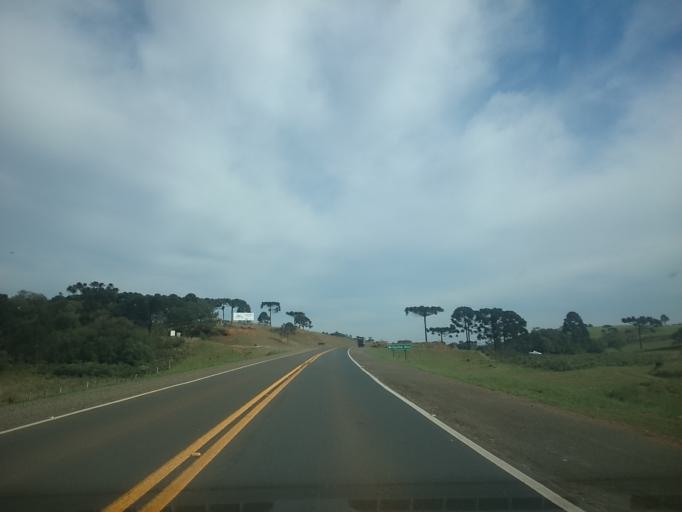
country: BR
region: Rio Grande do Sul
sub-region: Vacaria
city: Estrela
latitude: -28.0753
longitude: -50.5805
